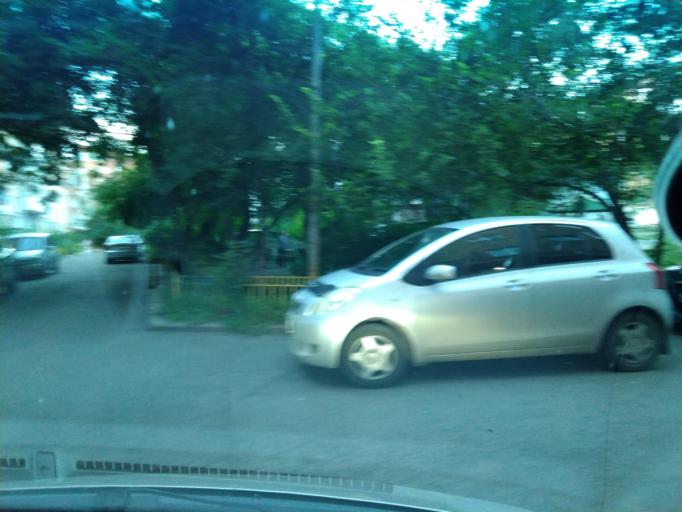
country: RU
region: Krasnoyarskiy
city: Krasnoyarsk
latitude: 56.0137
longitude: 92.8486
